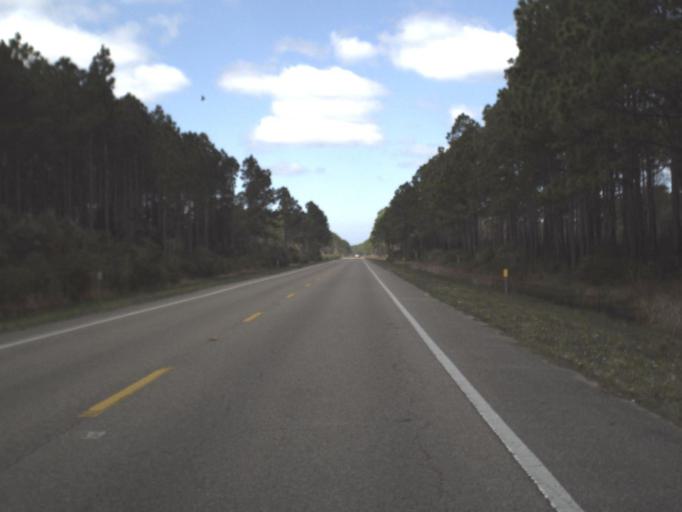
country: US
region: Florida
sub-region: Franklin County
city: Apalachicola
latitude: 29.7281
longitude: -85.1321
